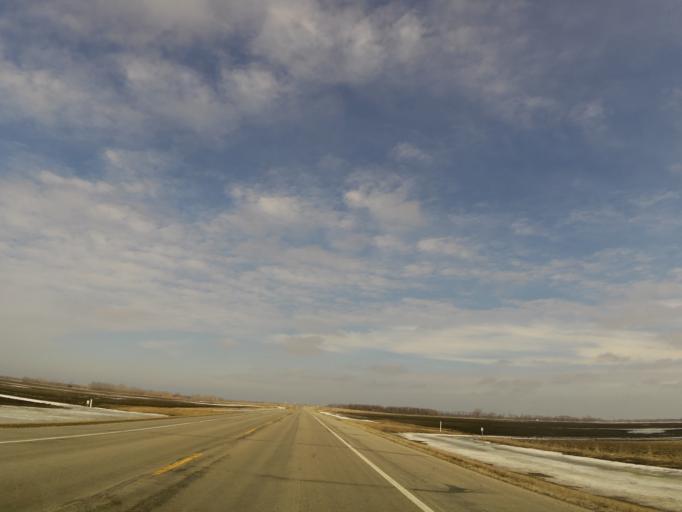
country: US
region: North Dakota
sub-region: Walsh County
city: Grafton
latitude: 48.4119
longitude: -97.2026
